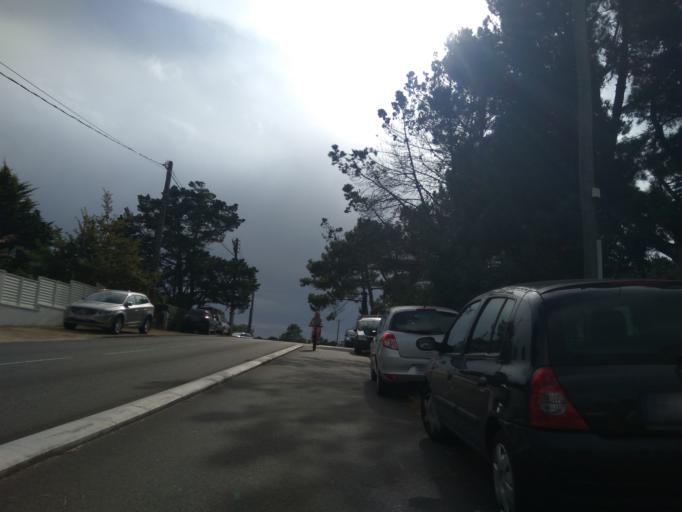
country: FR
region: Aquitaine
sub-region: Departement des Landes
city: Capbreton
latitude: 43.6447
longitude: -1.4408
